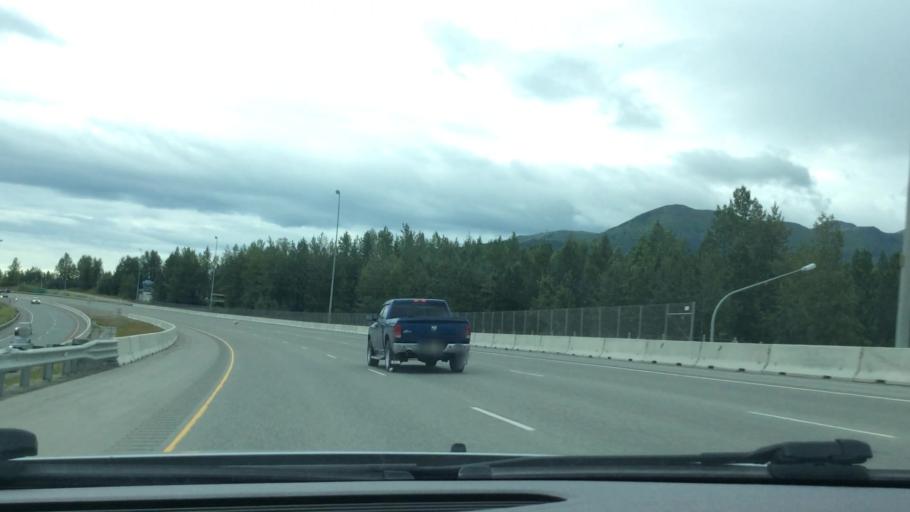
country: US
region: Alaska
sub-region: Anchorage Municipality
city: Eagle River
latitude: 61.3117
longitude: -149.5769
